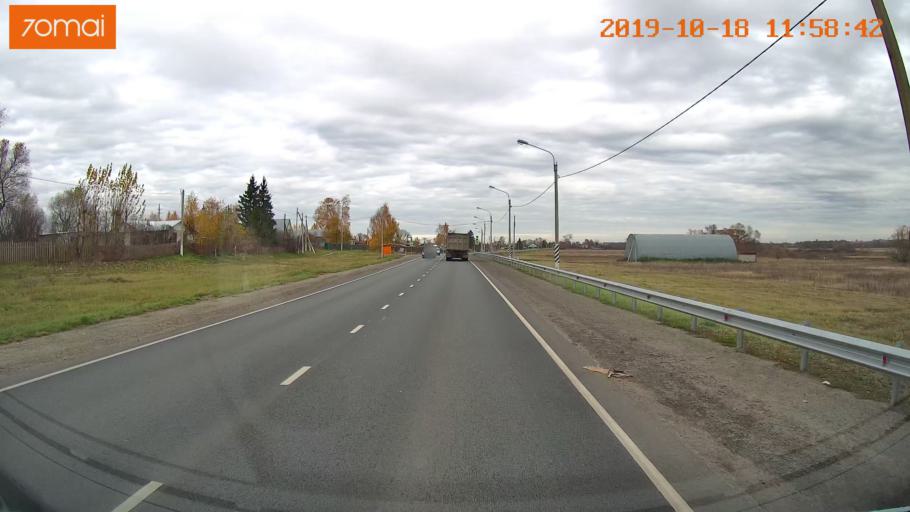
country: RU
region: Rjazan
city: Zakharovo
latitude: 54.2744
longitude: 39.1691
